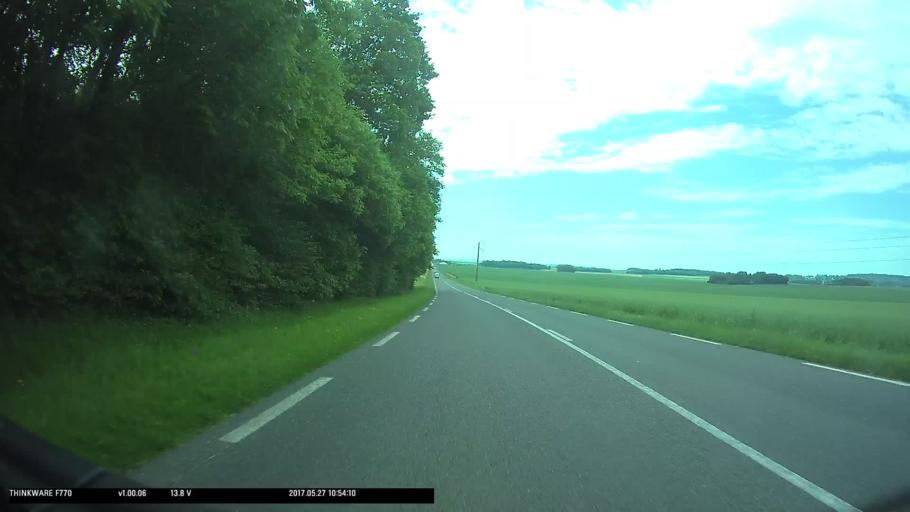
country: FR
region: Picardie
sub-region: Departement de l'Oise
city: Chaumont-en-Vexin
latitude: 49.2127
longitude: 1.8817
